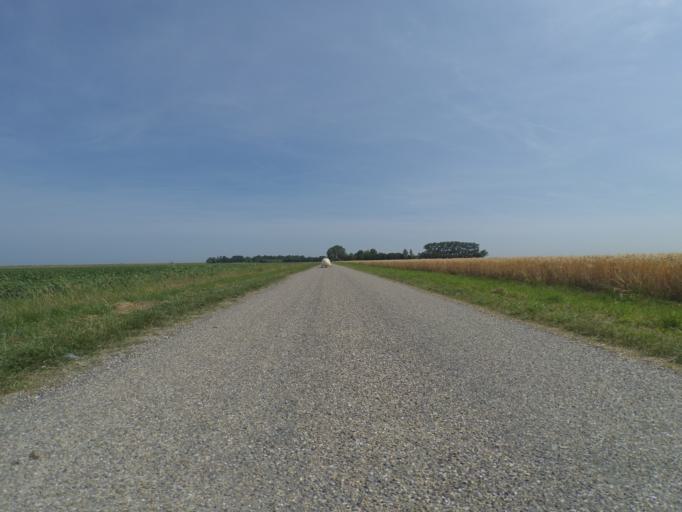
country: NL
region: Zeeland
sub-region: Schouwen-Duiveland
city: Bruinisse
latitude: 51.6405
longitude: 4.1310
